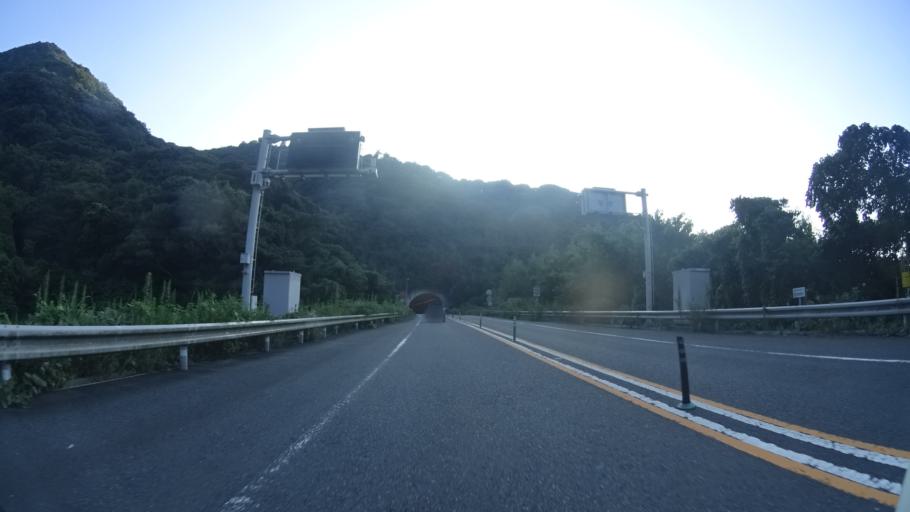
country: JP
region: Yamaguchi
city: Nagato
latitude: 34.3760
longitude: 131.2781
